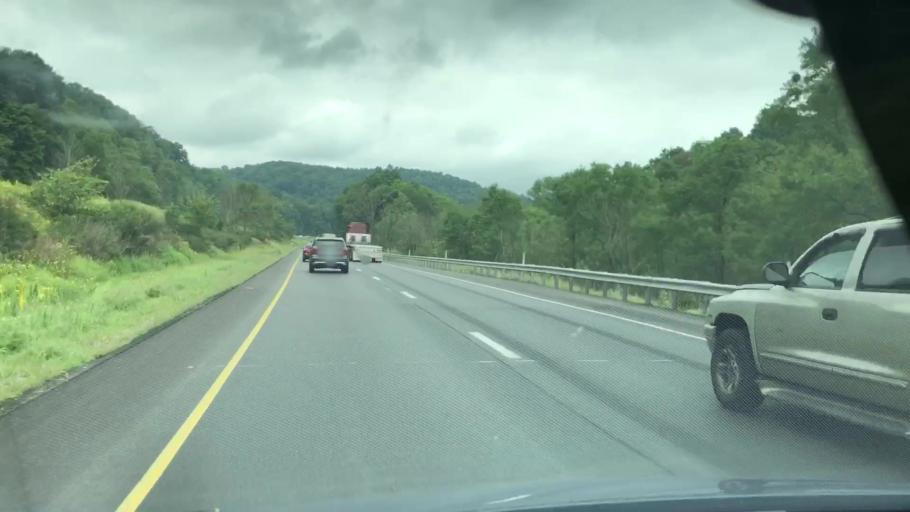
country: US
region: Pennsylvania
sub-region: Butler County
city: Zelienople
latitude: 40.8295
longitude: -80.1025
